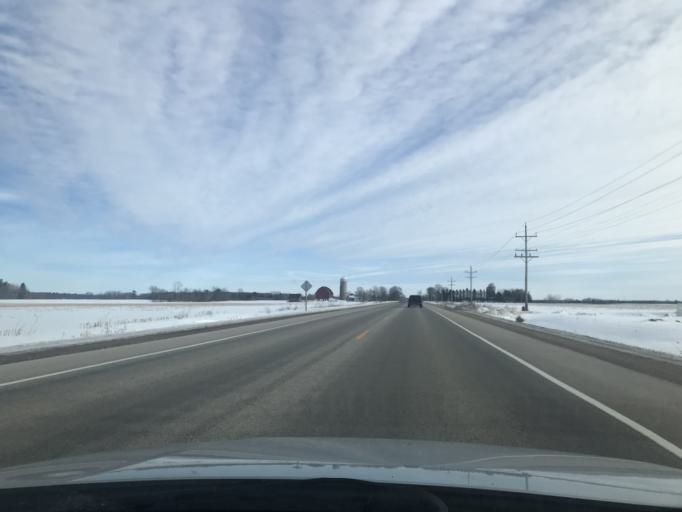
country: US
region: Wisconsin
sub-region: Oconto County
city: Gillett
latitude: 44.8963
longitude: -88.2751
